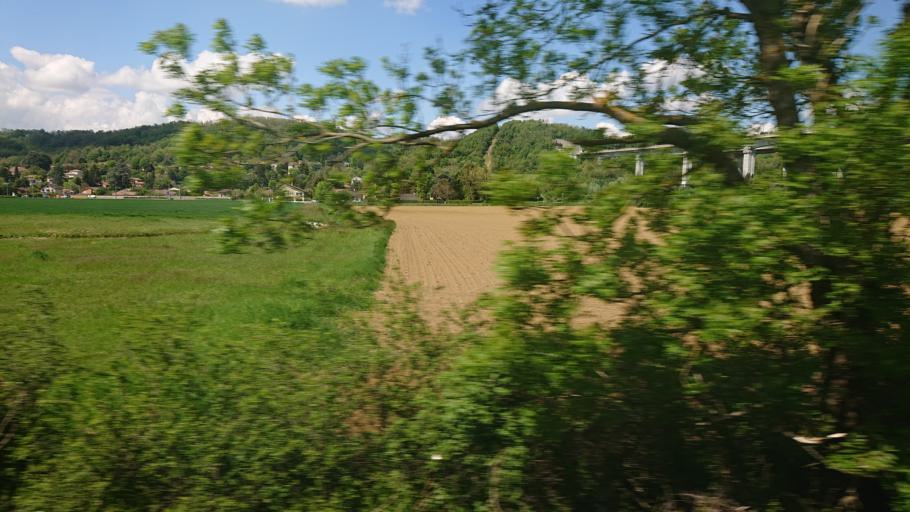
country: FR
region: Rhone-Alpes
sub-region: Departement de l'Ain
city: Beynost
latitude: 45.8358
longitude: 5.0154
